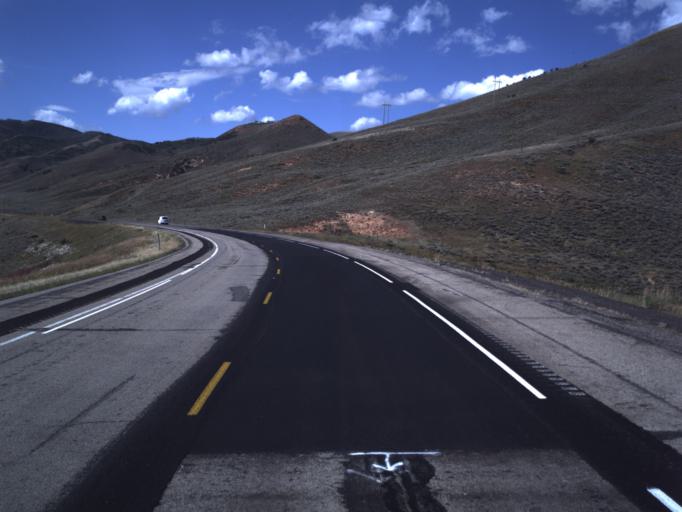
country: US
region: Utah
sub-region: Wasatch County
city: Heber
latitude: 40.2112
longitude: -111.1023
